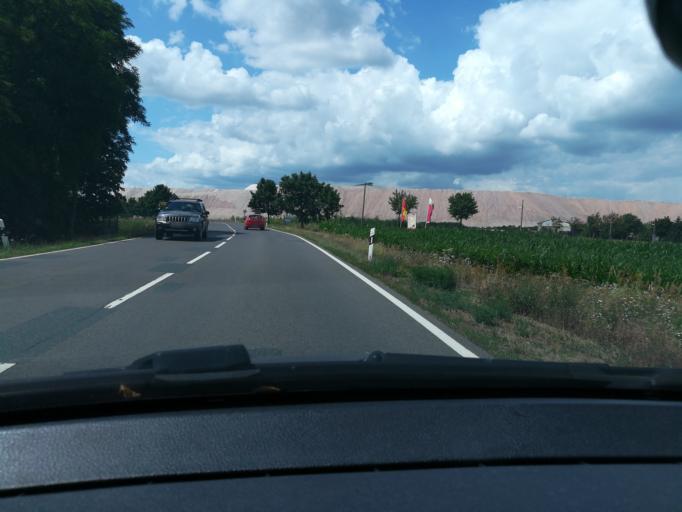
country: DE
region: Saxony-Anhalt
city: Zielitz
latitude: 52.3016
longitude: 11.7050
